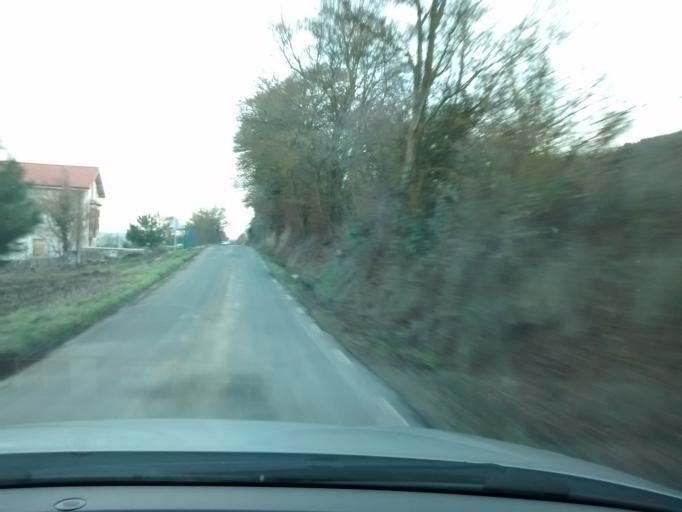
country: ES
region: Castille and Leon
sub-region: Provincia de Burgos
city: Espinosa de los Monteros
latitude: 43.0453
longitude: -3.5222
